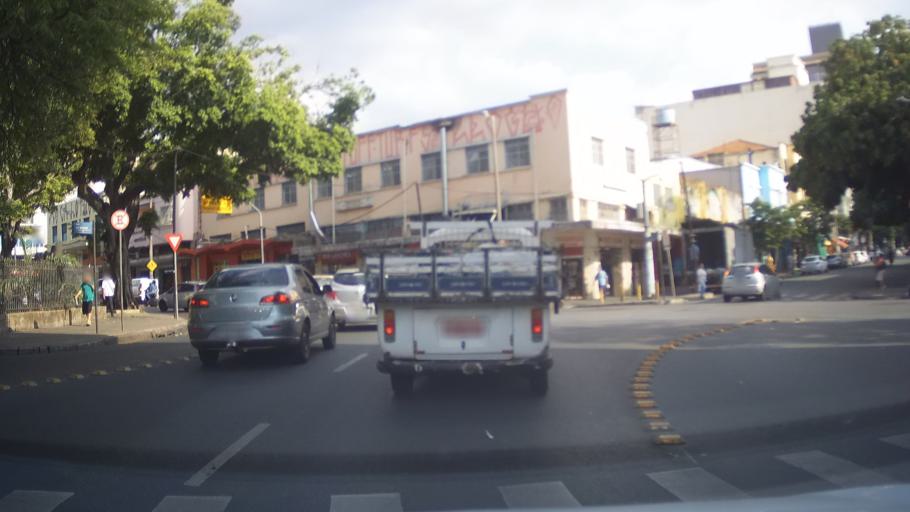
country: BR
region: Minas Gerais
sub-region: Belo Horizonte
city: Belo Horizonte
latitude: -19.9154
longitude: -43.9424
